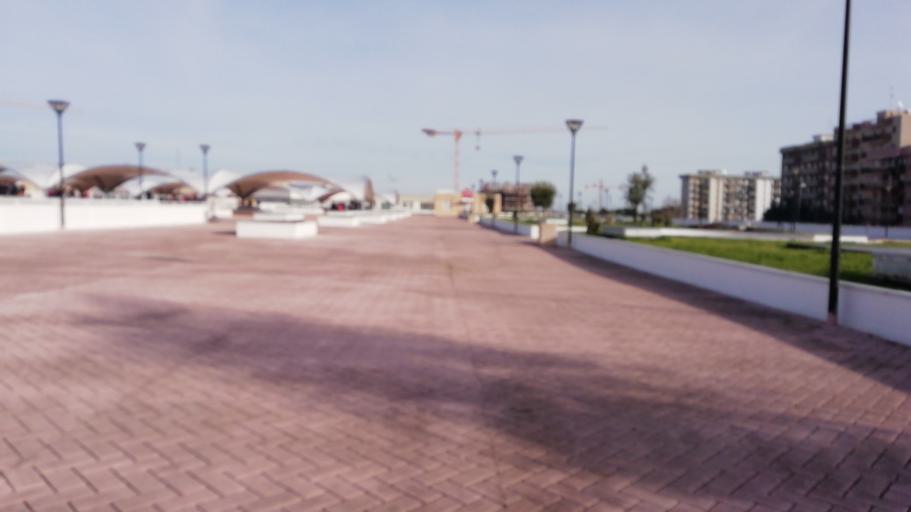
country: IT
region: Apulia
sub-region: Provincia di Bari
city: Triggiano
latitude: 41.1042
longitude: 16.9116
